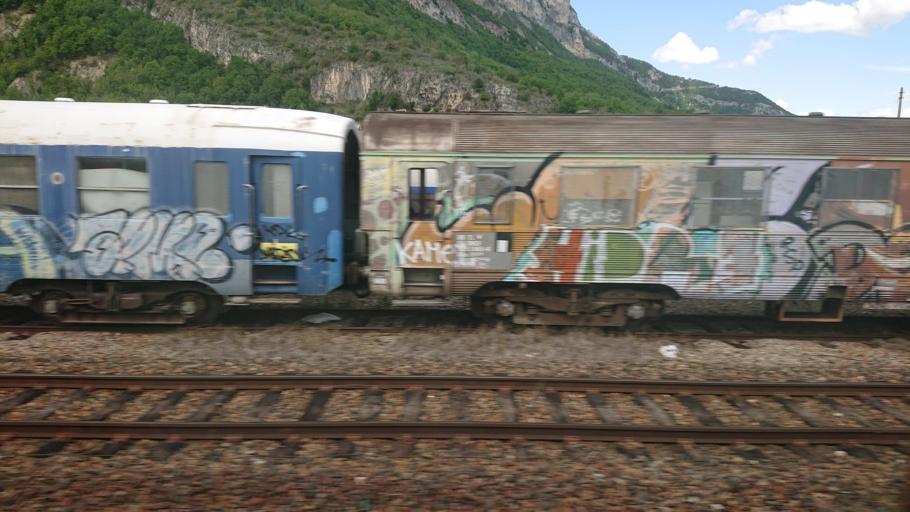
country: FR
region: Rhone-Alpes
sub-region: Departement de l'Ain
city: Culoz
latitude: 45.8467
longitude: 5.7650
